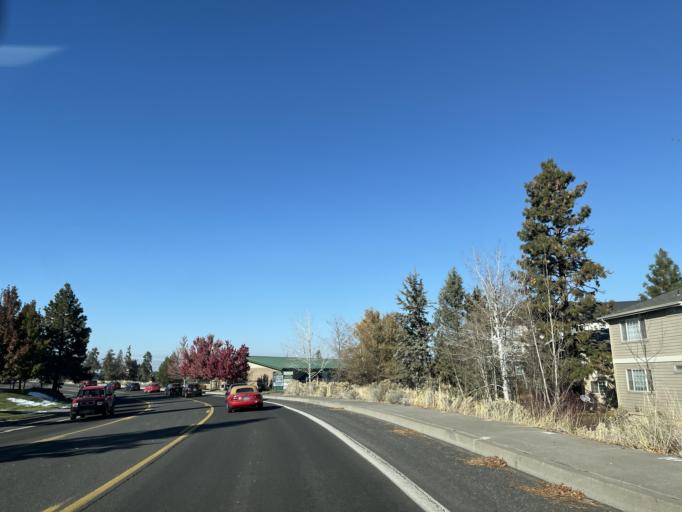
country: US
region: Oregon
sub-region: Deschutes County
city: Bend
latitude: 44.0770
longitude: -121.2981
